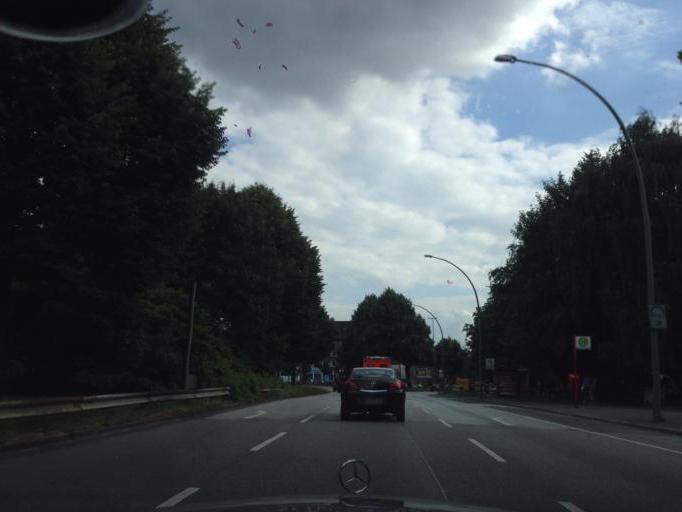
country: DE
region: Hamburg
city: Marienthal
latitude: 53.5546
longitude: 10.0836
